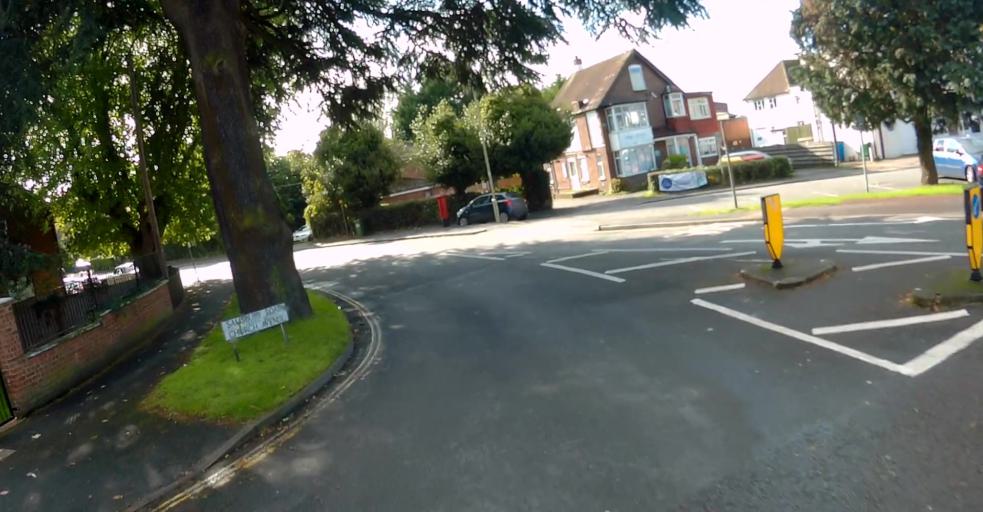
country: GB
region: England
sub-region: Hampshire
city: Farnborough
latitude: 51.2940
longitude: -0.7523
